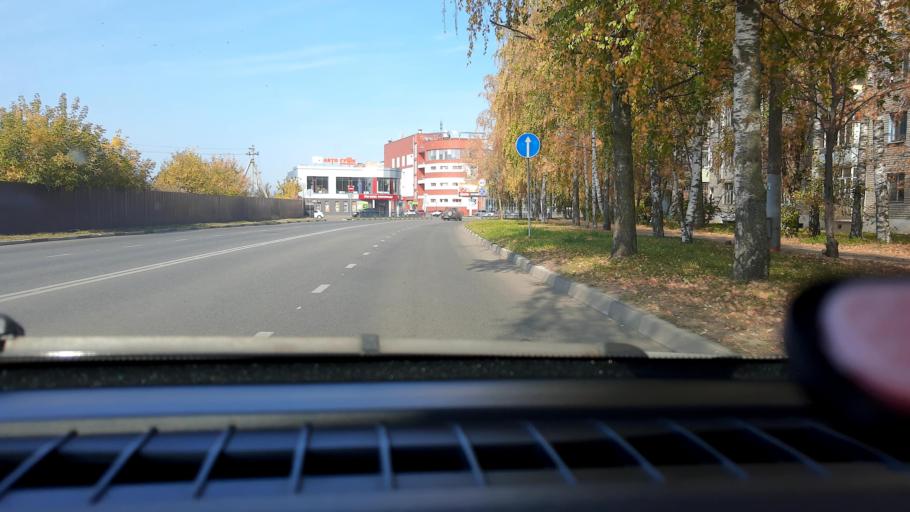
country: RU
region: Nizjnij Novgorod
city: Kstovo
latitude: 56.1443
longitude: 44.1797
